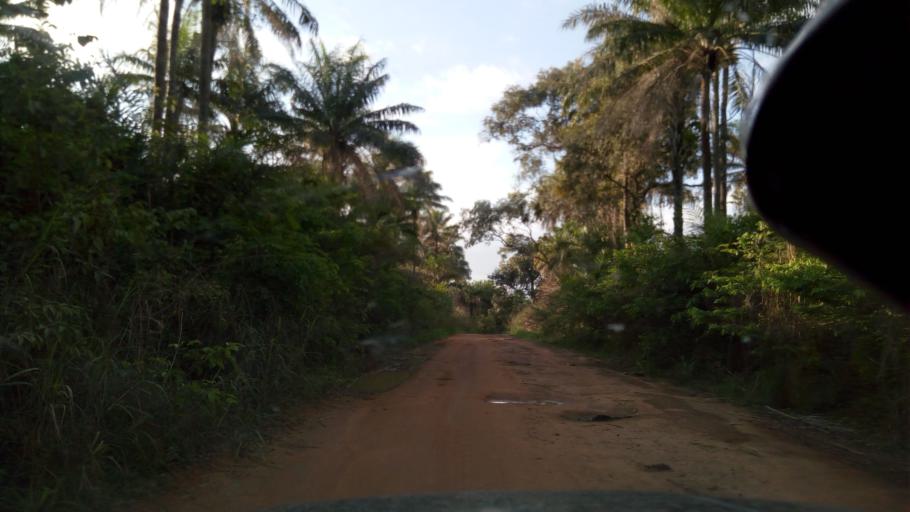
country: SL
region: Northern Province
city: Konakridee
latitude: 8.7538
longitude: -13.1433
